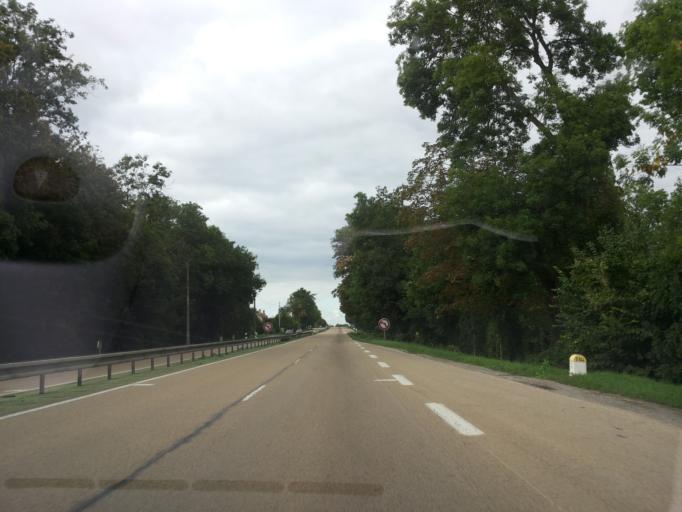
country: FR
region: Champagne-Ardenne
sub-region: Departement de la Marne
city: Verzy
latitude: 49.1180
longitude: 4.2499
